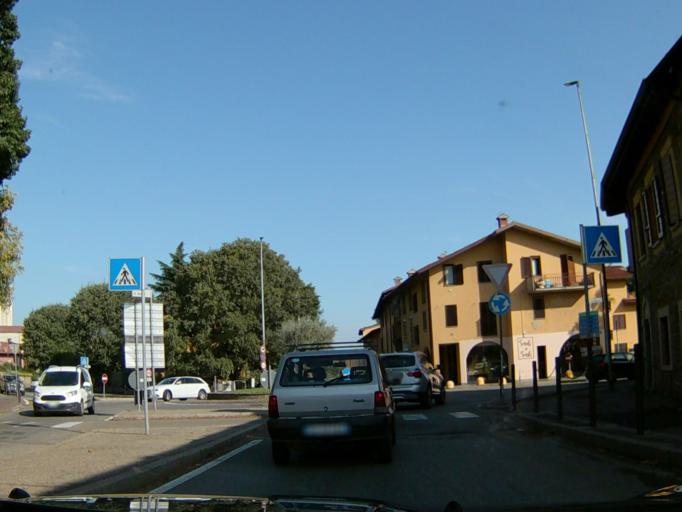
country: IT
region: Lombardy
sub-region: Provincia di Brescia
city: Coccaglio
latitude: 45.5638
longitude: 9.9738
